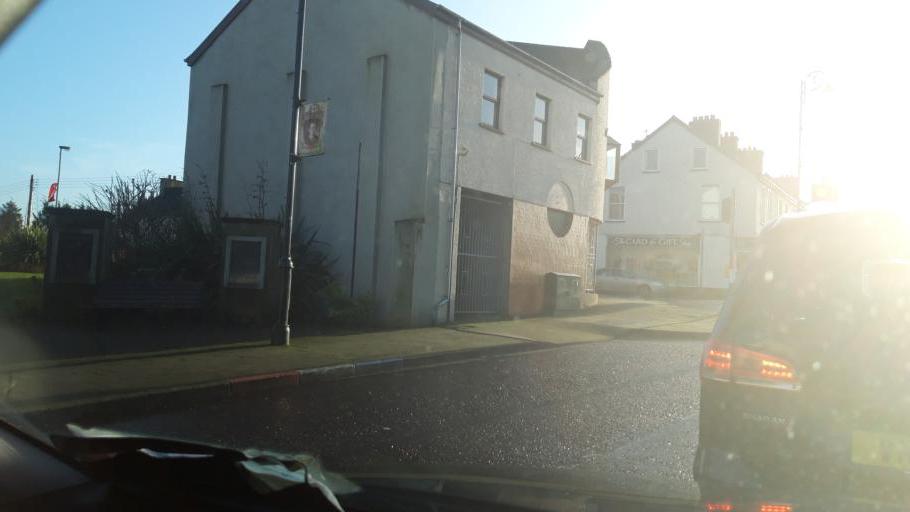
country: GB
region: Northern Ireland
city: Garvagh
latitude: 54.9837
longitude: -6.6874
